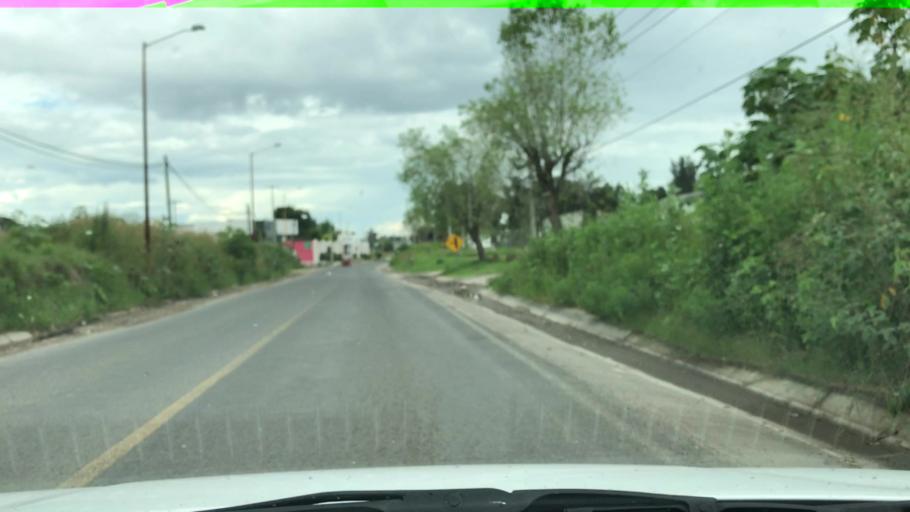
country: MX
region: Jalisco
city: Nicolas R Casillas
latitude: 20.5465
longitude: -103.4805
